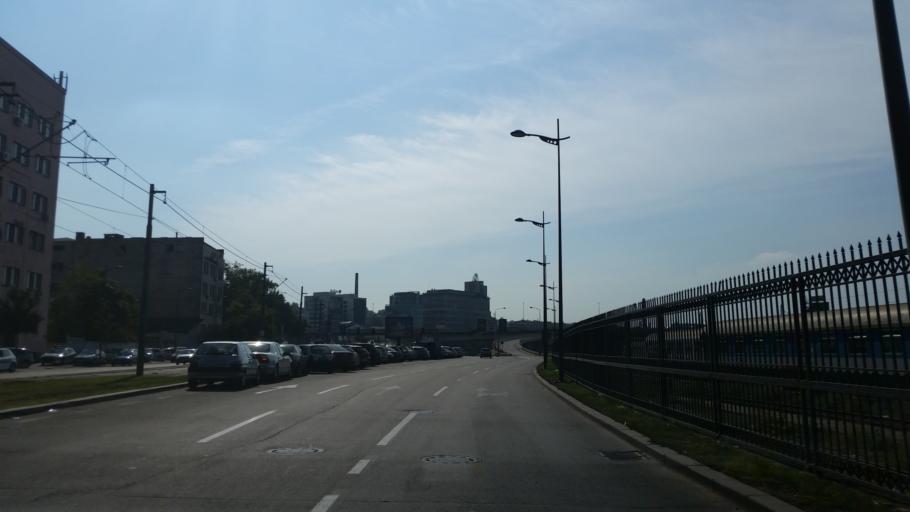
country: RS
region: Central Serbia
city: Belgrade
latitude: 44.8018
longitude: 20.4509
